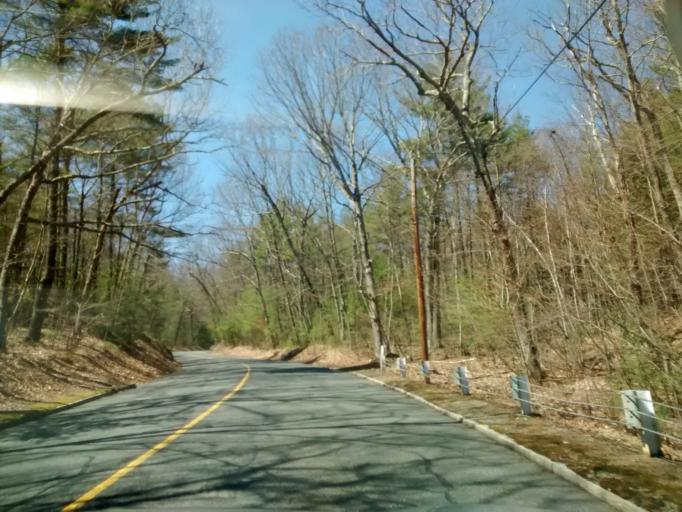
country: US
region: Massachusetts
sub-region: Worcester County
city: Whitinsville
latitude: 42.1280
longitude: -71.7096
